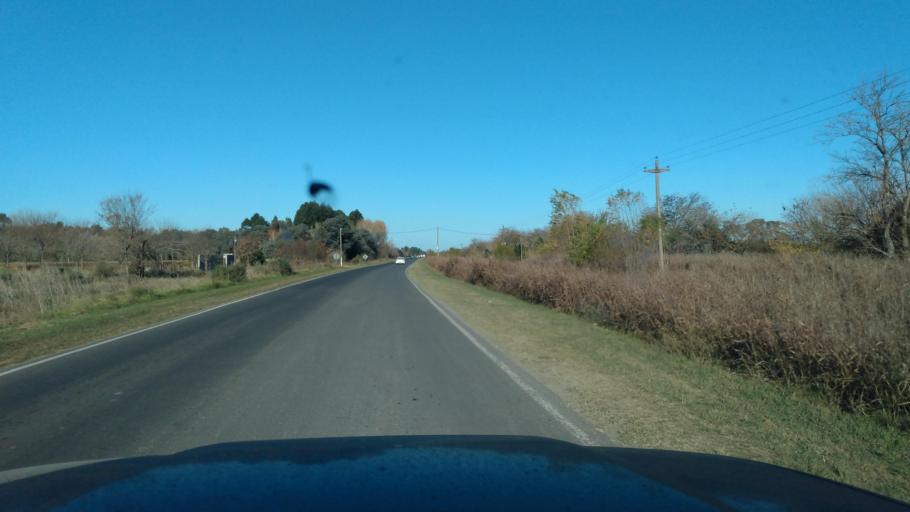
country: AR
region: Buenos Aires
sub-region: Partido de Lujan
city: Lujan
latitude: -34.4969
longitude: -59.2049
